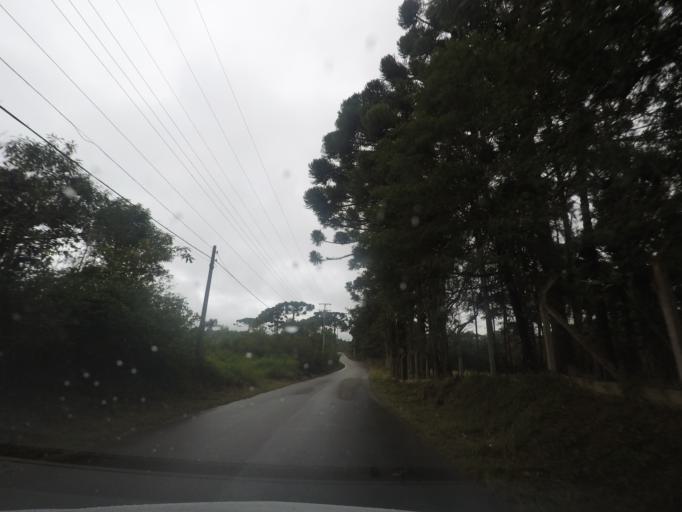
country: BR
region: Parana
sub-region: Campina Grande Do Sul
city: Campina Grande do Sul
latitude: -25.3029
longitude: -49.1314
